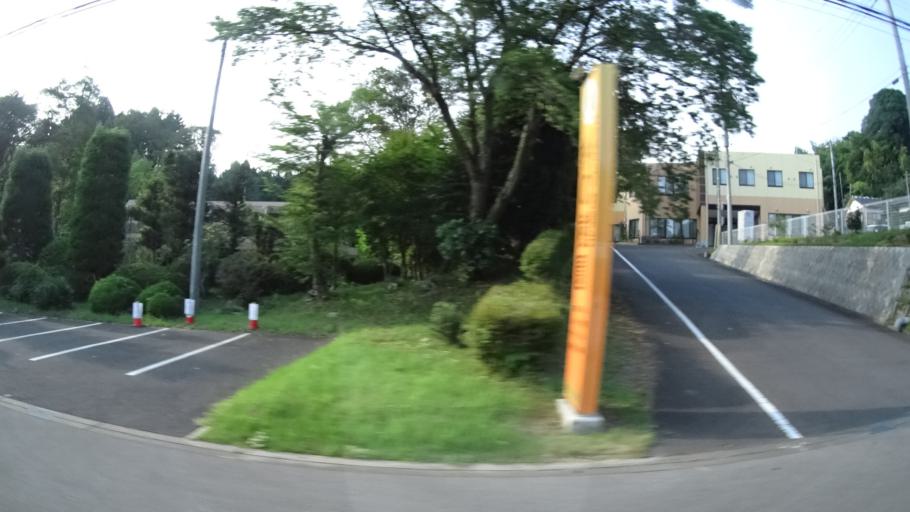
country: JP
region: Tochigi
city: Karasuyama
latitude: 36.5947
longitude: 140.1259
